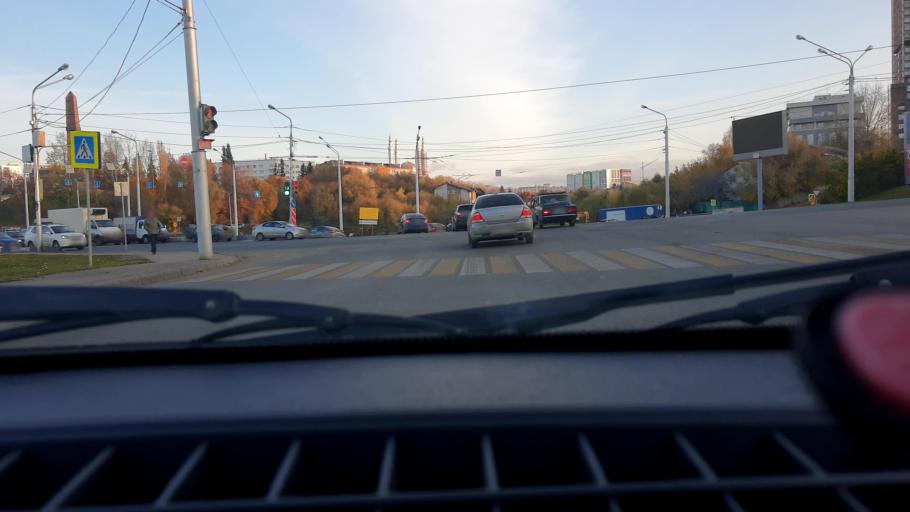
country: RU
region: Bashkortostan
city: Ufa
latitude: 54.7090
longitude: 55.9629
